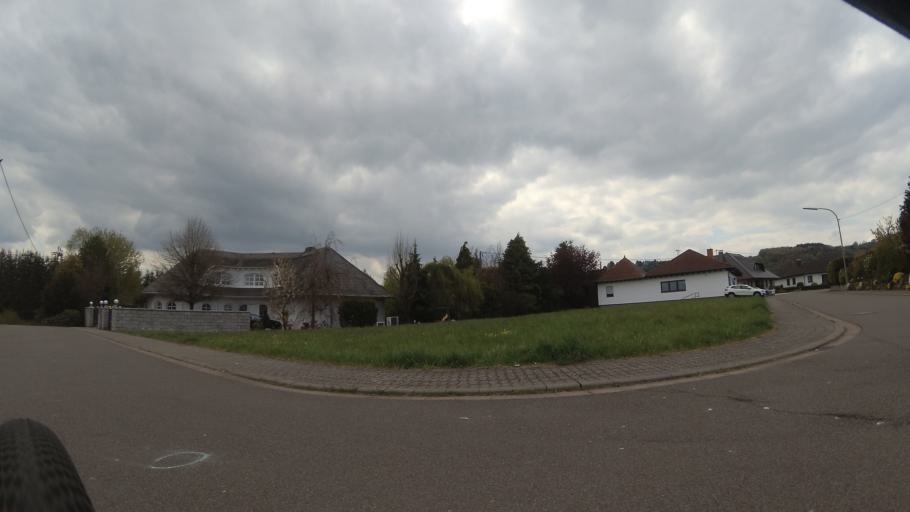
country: DE
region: Saarland
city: Losheim
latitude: 49.5054
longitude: 6.7566
